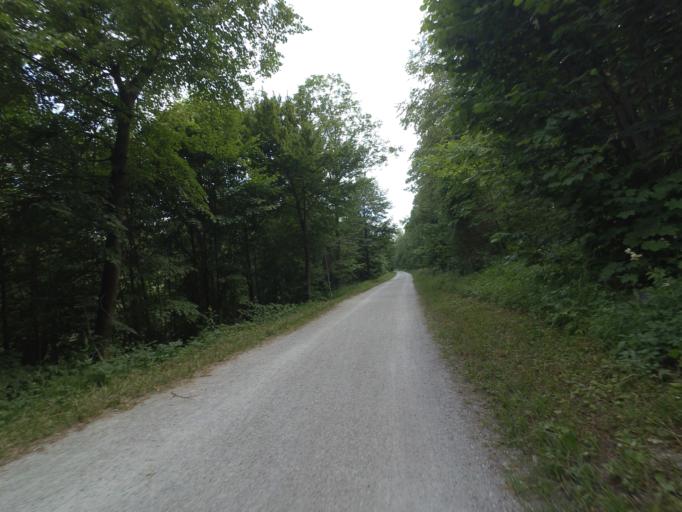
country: DE
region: Bavaria
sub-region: Upper Bavaria
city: Ainring
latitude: 47.7974
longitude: 12.9620
